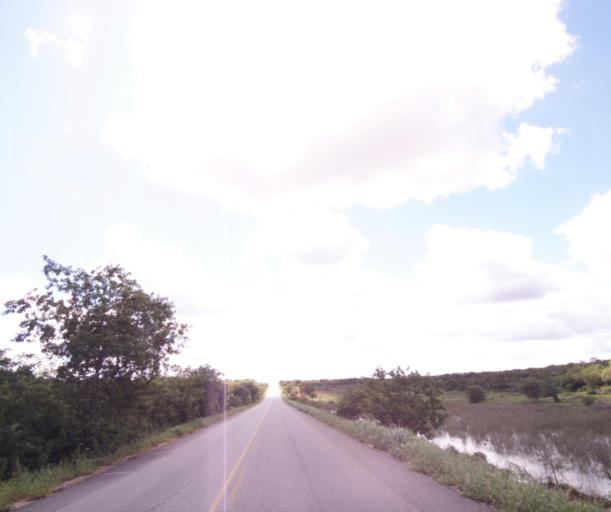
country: BR
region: Bahia
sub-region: Caetite
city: Caetite
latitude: -14.1675
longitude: -42.2404
